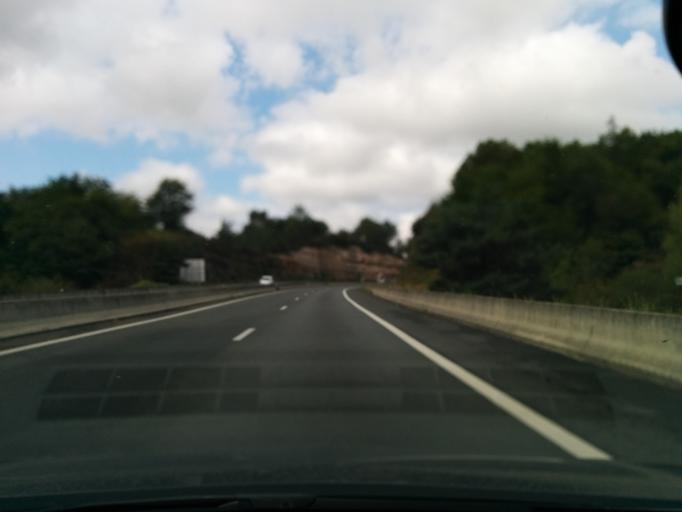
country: FR
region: Limousin
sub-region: Departement de la Correze
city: Brive-la-Gaillarde
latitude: 45.1106
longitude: 1.5037
